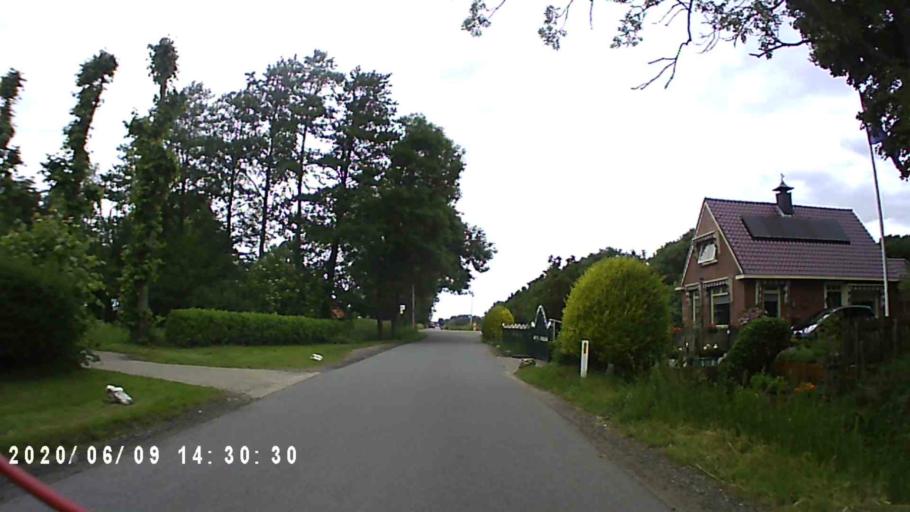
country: NL
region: Groningen
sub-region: Gemeente Bedum
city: Bedum
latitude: 53.3126
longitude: 6.5934
